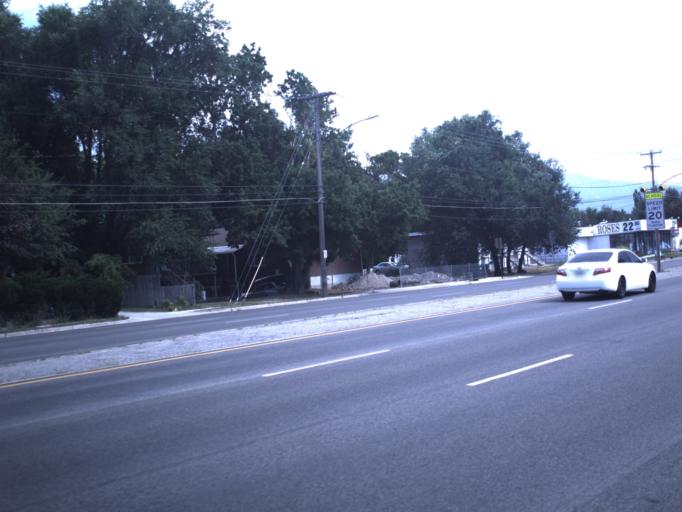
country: US
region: Utah
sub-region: Salt Lake County
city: South Salt Lake
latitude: 40.7140
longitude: -111.8715
